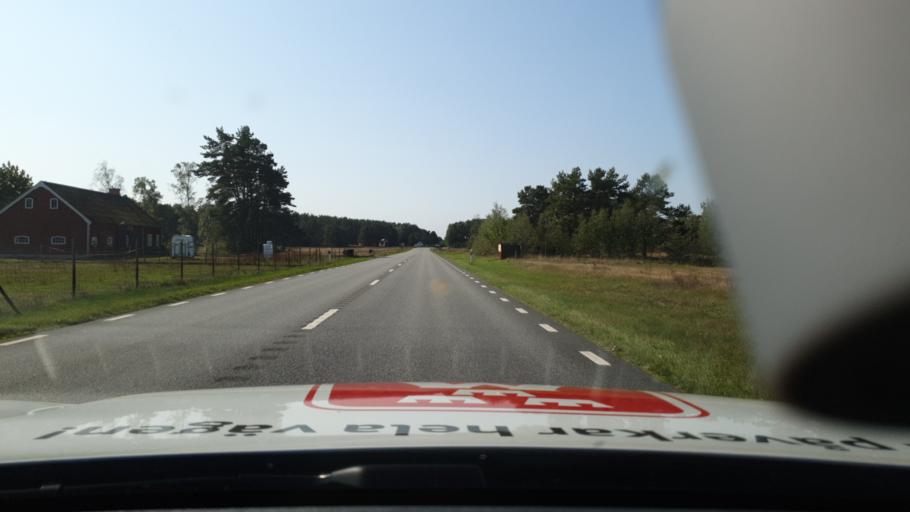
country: SE
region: Skane
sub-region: Kristianstads Kommun
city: Ahus
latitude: 55.8935
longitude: 14.2480
